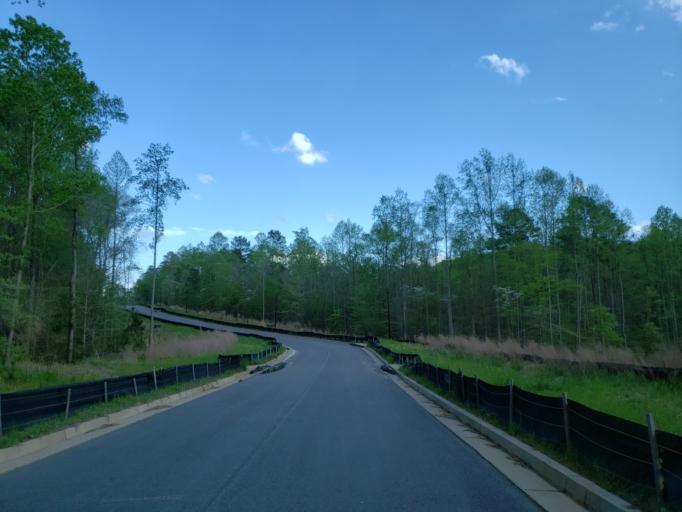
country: US
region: Georgia
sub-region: Fulton County
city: Roswell
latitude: 34.1110
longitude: -84.3965
